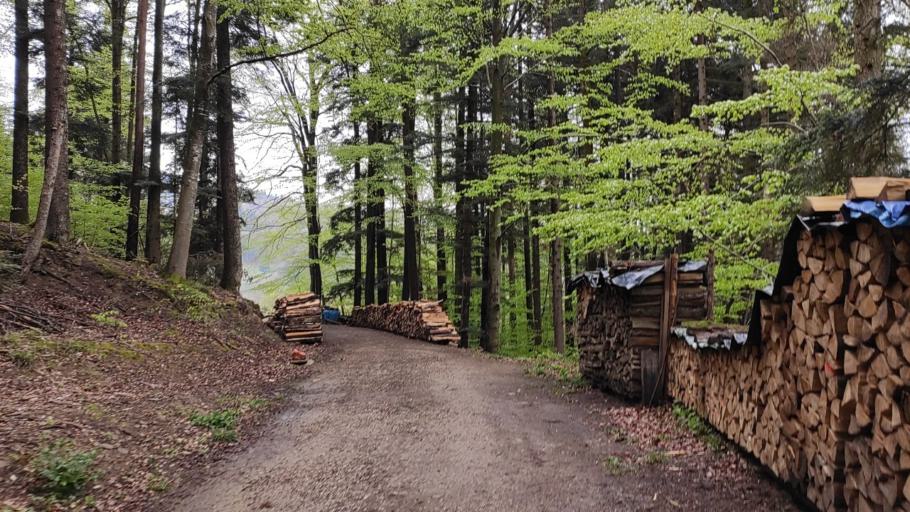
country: DE
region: Baden-Wuerttemberg
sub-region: Freiburg Region
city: Solden
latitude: 47.9125
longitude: 7.8365
